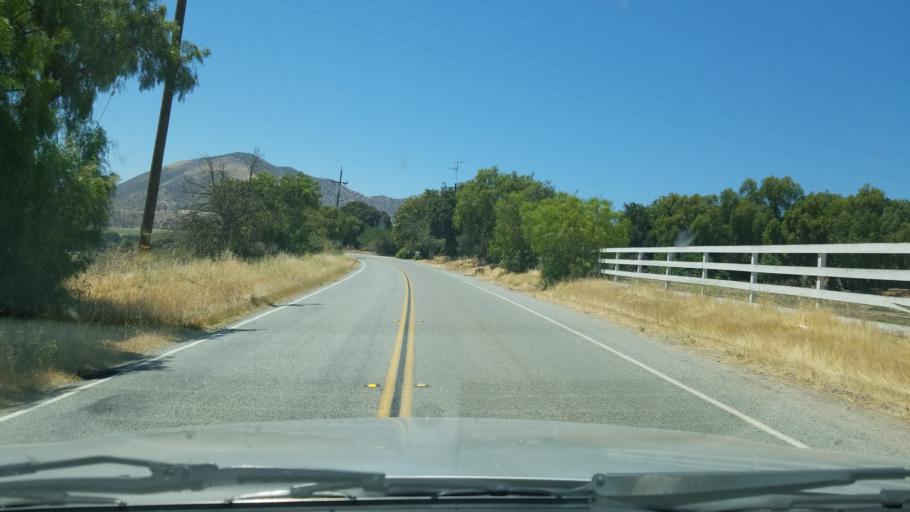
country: US
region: California
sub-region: Monterey County
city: Greenfield
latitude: 36.3015
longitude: -121.3131
